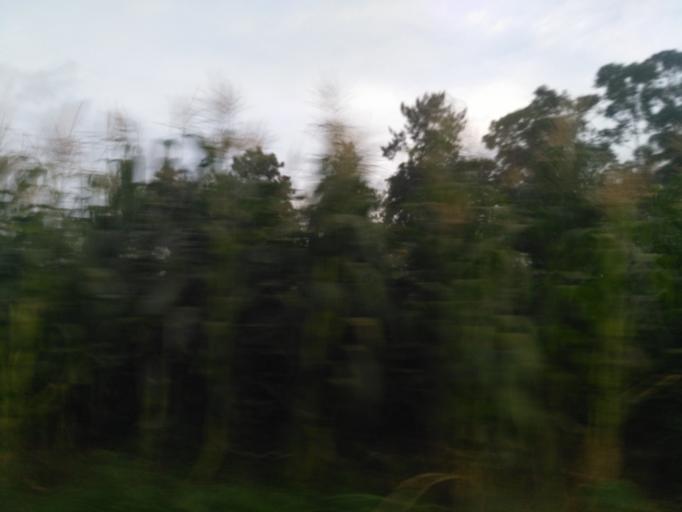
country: UG
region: Eastern Region
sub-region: Jinja District
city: Jinja
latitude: 0.4303
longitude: 33.2009
